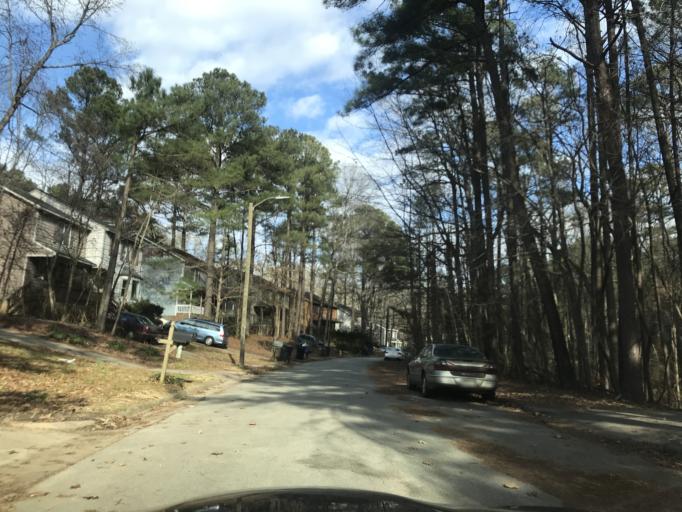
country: US
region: North Carolina
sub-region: Wake County
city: West Raleigh
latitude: 35.7707
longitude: -78.7200
